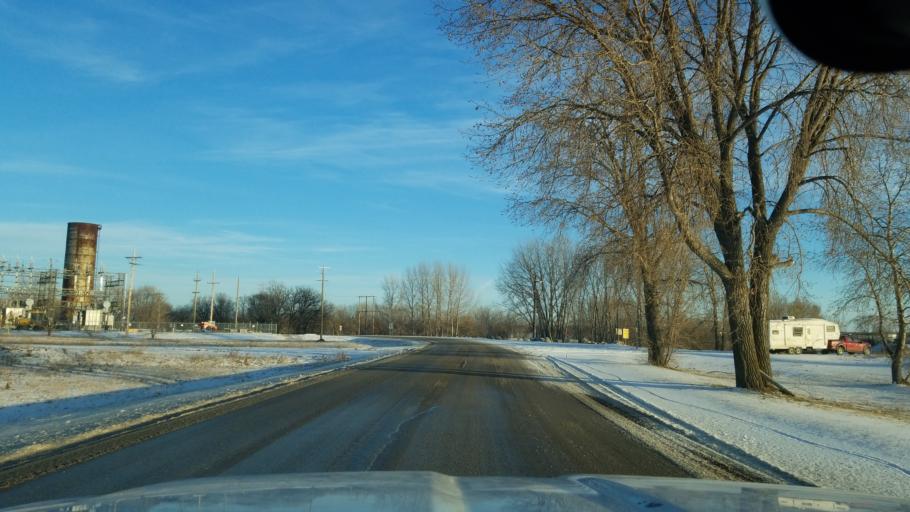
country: CA
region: Manitoba
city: Portage la Prairie
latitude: 49.9495
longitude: -98.3335
